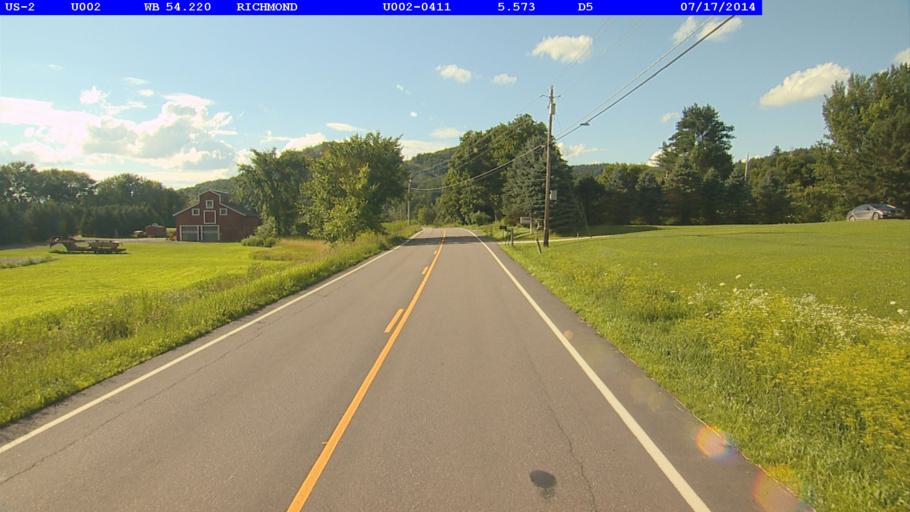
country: US
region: Vermont
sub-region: Chittenden County
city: Jericho
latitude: 44.3906
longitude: -72.9441
